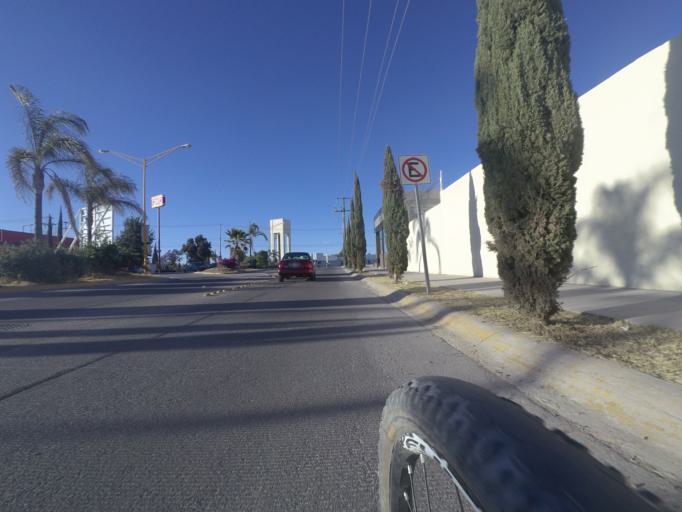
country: MX
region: Aguascalientes
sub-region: Aguascalientes
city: La Loma de los Negritos
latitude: 21.8571
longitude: -102.3453
